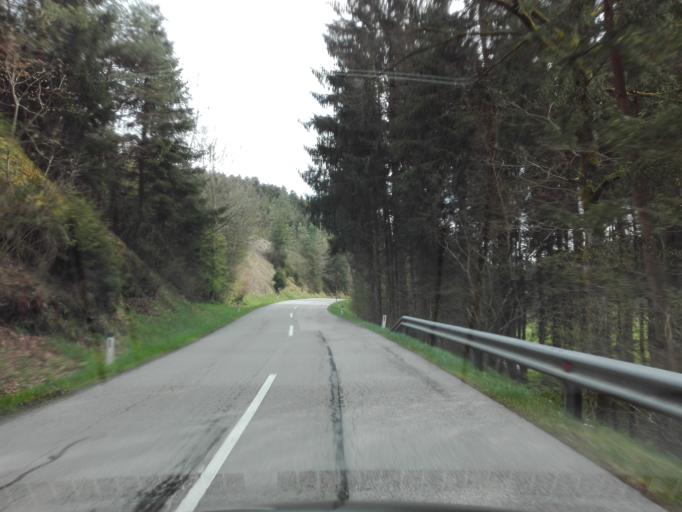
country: AT
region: Upper Austria
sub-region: Politischer Bezirk Rohrbach
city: Atzesberg
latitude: 48.5299
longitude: 13.9451
